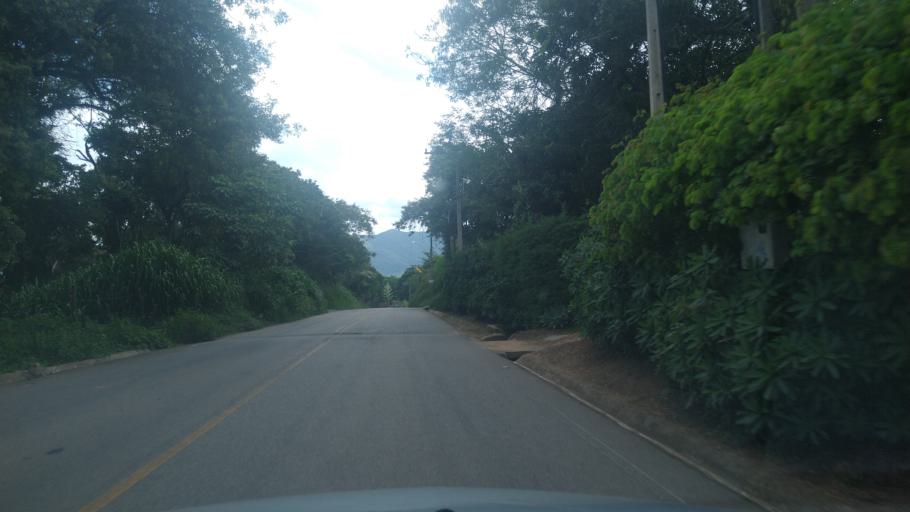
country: BR
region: Minas Gerais
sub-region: Extrema
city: Extrema
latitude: -22.8052
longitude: -46.3143
